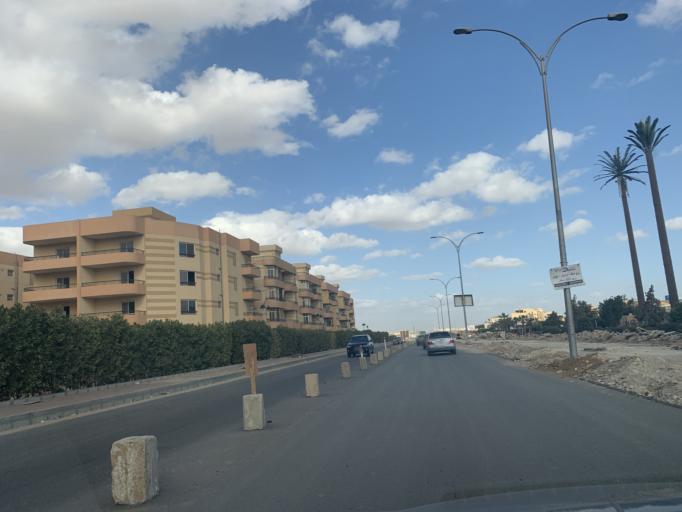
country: EG
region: Al Jizah
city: Madinat Sittah Uktubar
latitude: 29.9867
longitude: 30.9388
